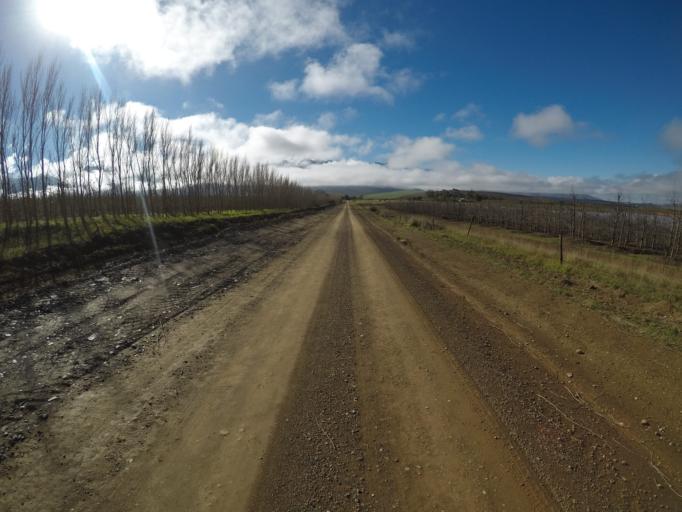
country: ZA
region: Western Cape
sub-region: Overberg District Municipality
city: Caledon
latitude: -34.1167
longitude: 19.7391
